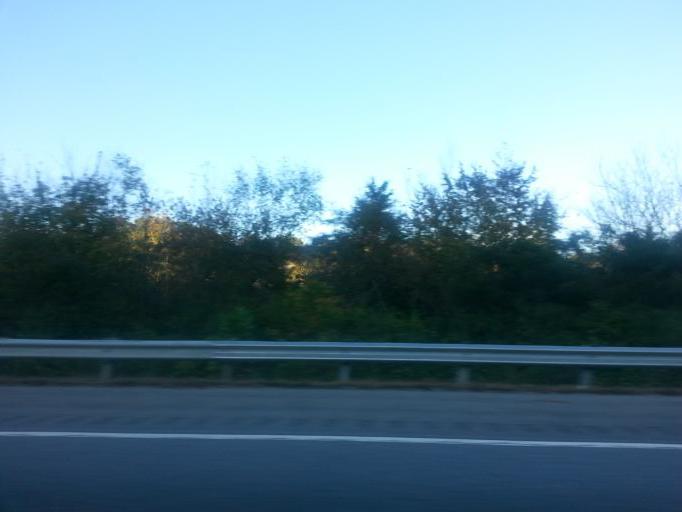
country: US
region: Tennessee
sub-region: Anderson County
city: Norris
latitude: 36.1801
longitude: -84.0930
